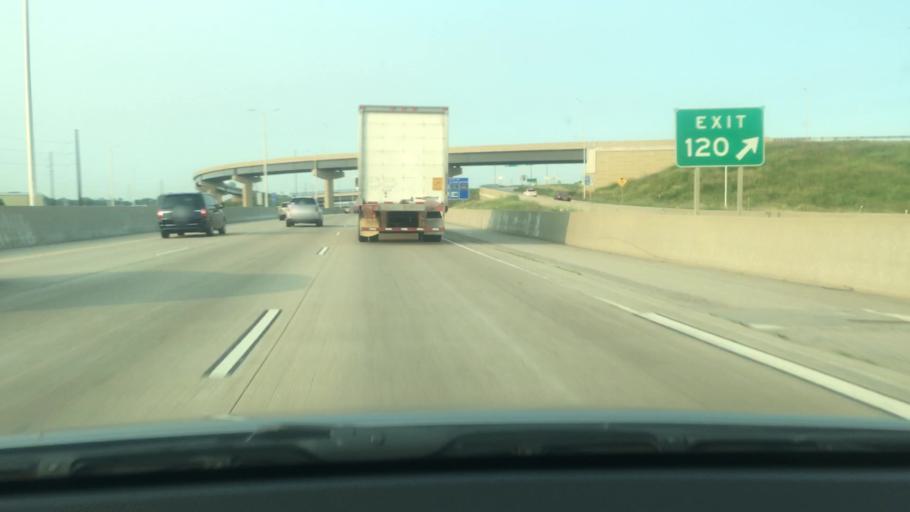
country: US
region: Wisconsin
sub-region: Winnebago County
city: Oshkosh
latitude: 44.0631
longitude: -88.5720
